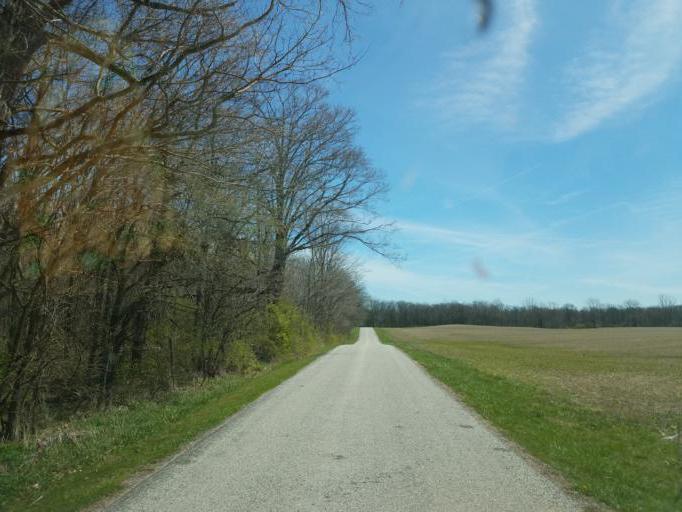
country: US
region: Ohio
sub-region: Delaware County
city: Ashley
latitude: 40.4292
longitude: -83.0646
